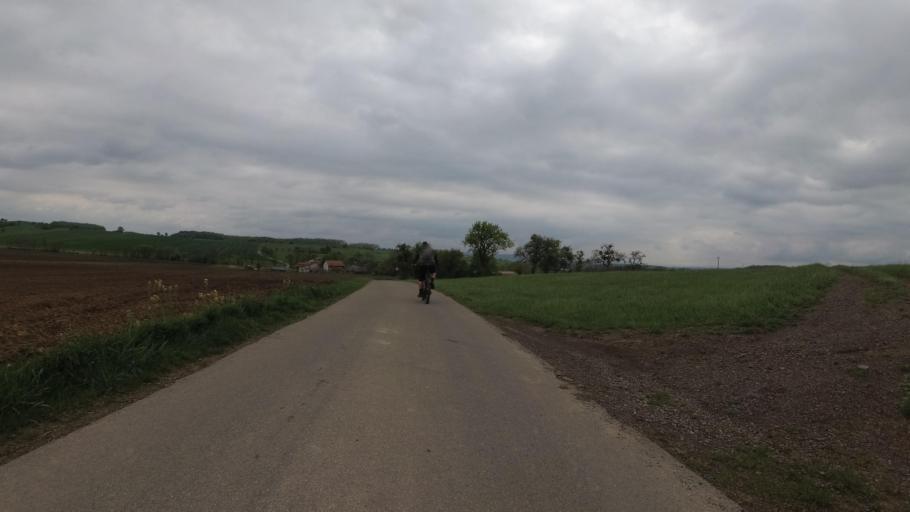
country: DE
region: Saarland
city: Merzig
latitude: 49.3912
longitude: 6.5915
